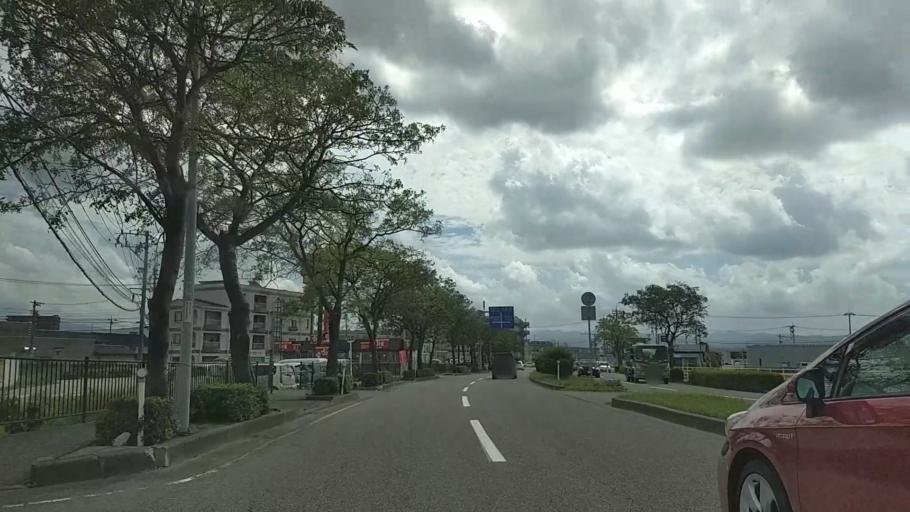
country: JP
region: Ishikawa
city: Kanazawa-shi
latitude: 36.5965
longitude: 136.6623
